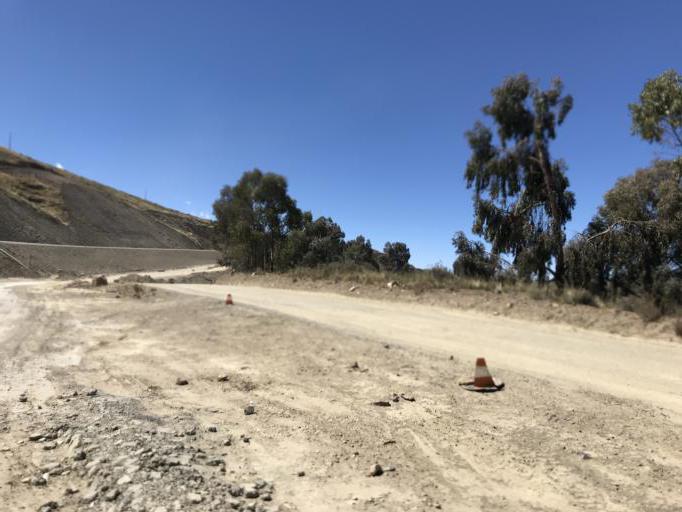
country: BO
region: La Paz
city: San Pablo
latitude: -16.1991
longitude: -68.8303
